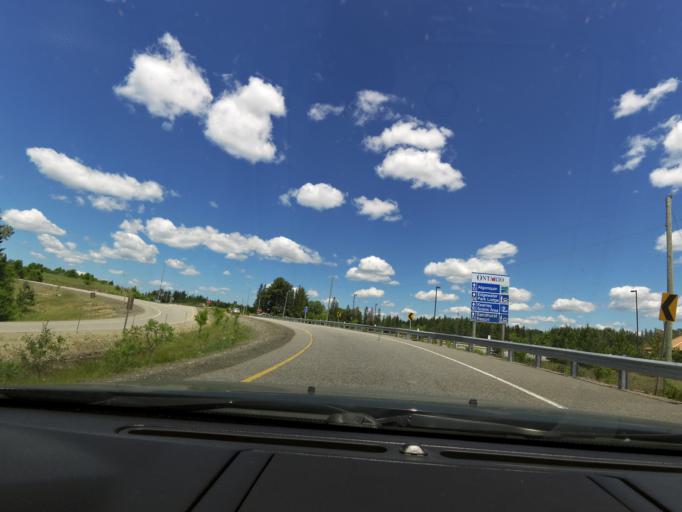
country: CA
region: Ontario
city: Huntsville
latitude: 45.5112
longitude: -79.3039
